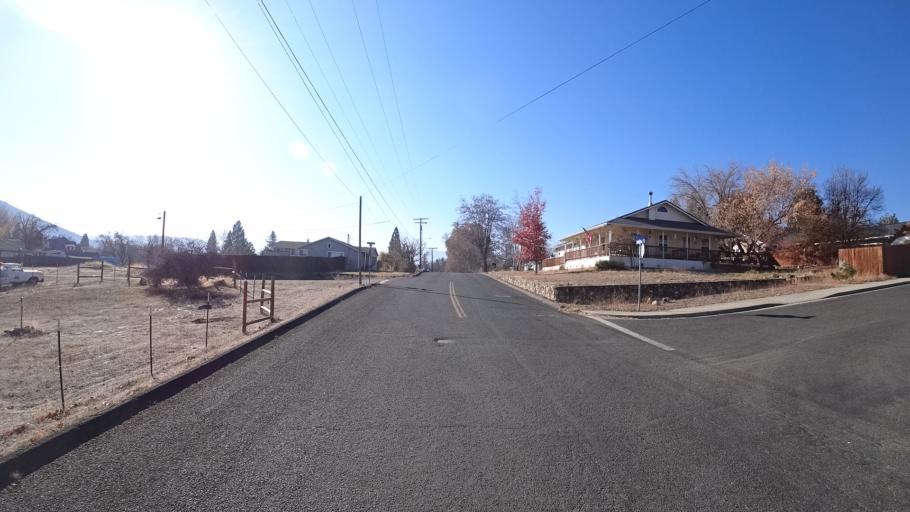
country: US
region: California
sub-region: Siskiyou County
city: Yreka
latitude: 41.7333
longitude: -122.6461
